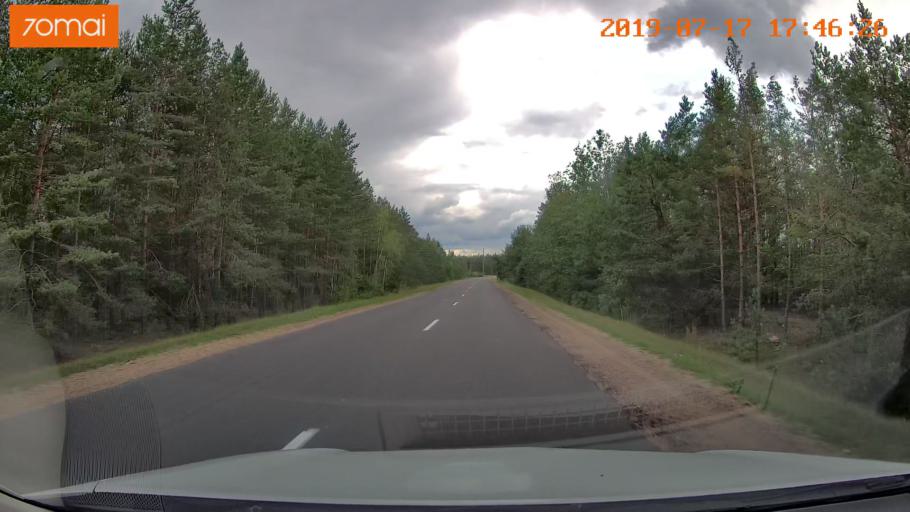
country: BY
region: Mogilev
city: Hlusha
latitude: 53.0984
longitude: 28.8405
